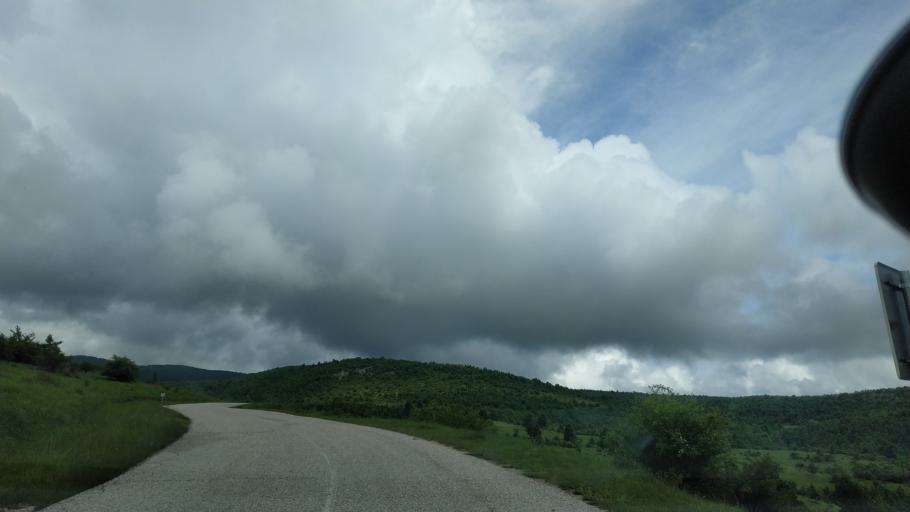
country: RS
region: Central Serbia
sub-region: Zajecarski Okrug
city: Soko Banja
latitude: 43.7091
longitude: 21.9406
